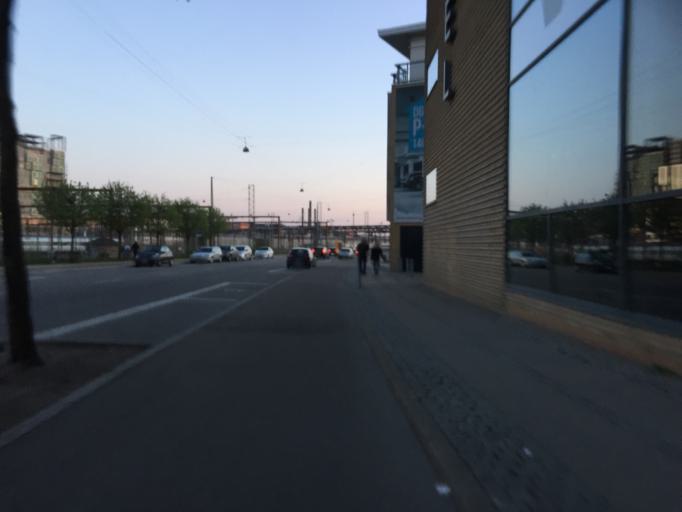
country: DK
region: Capital Region
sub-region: Kobenhavn
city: Copenhagen
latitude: 55.6689
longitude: 12.5649
